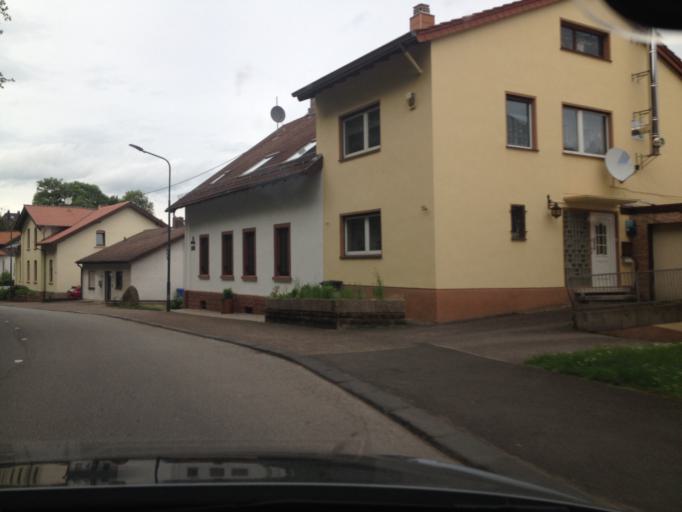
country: DE
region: Saarland
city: Spiesen-Elversberg
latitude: 49.3246
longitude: 7.1402
